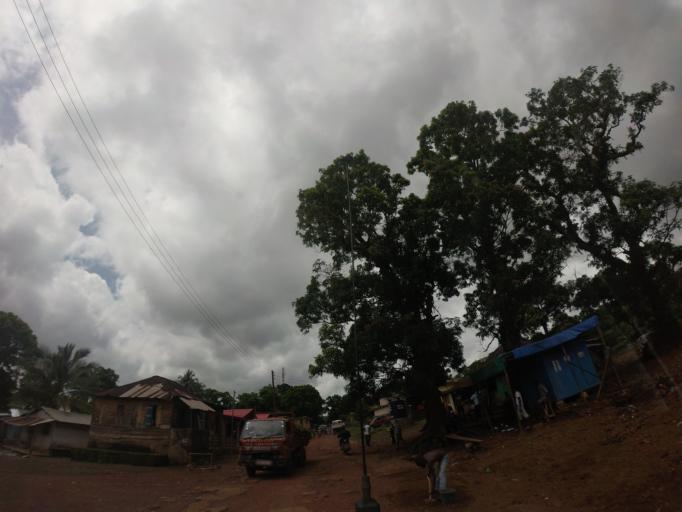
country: SL
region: Western Area
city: Hastings
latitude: 8.3828
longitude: -13.1415
